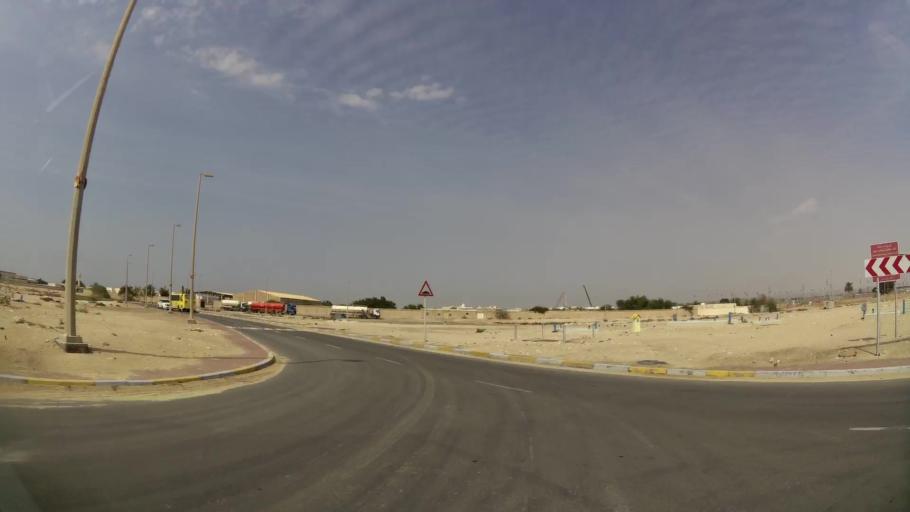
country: AE
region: Abu Dhabi
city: Abu Dhabi
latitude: 24.5607
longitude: 54.6840
